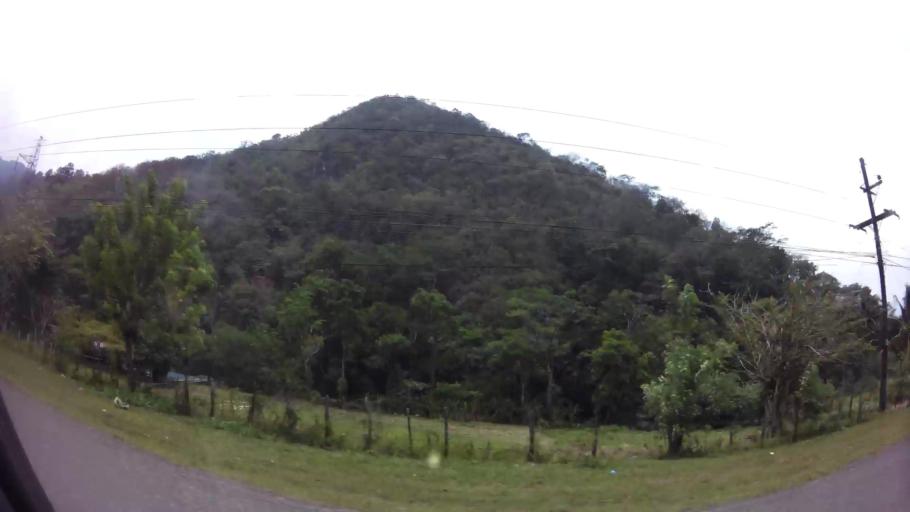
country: HN
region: Comayagua
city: Taulabe
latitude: 14.7284
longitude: -87.9633
